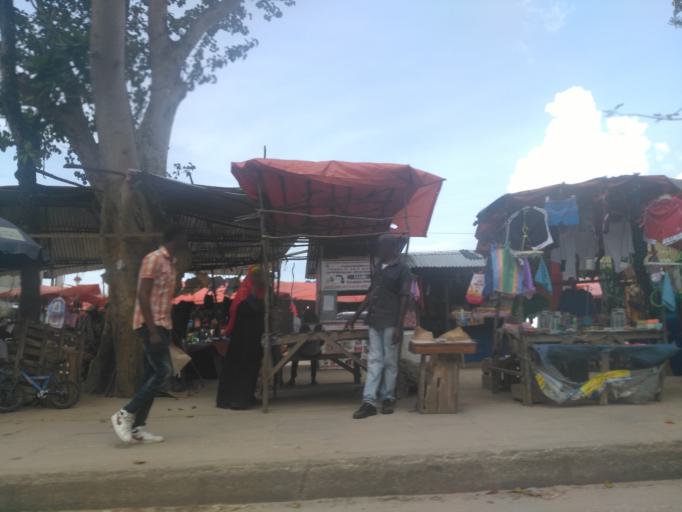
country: TZ
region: Zanzibar Urban/West
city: Zanzibar
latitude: -6.1558
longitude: 39.2059
